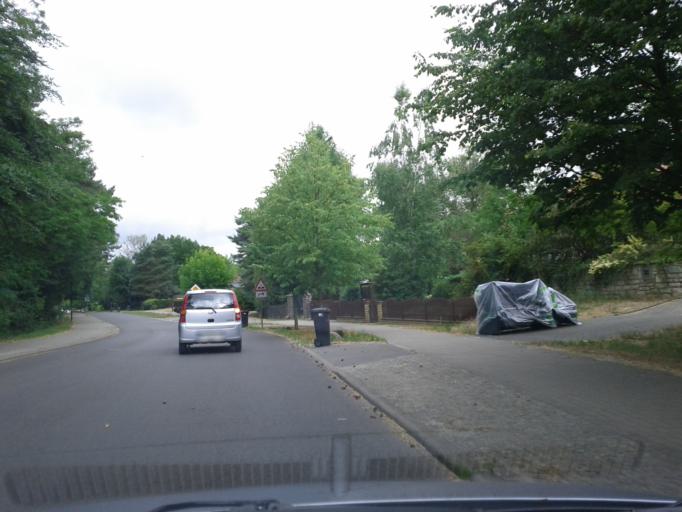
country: DE
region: Brandenburg
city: Woltersdorf
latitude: 52.4569
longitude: 13.7409
